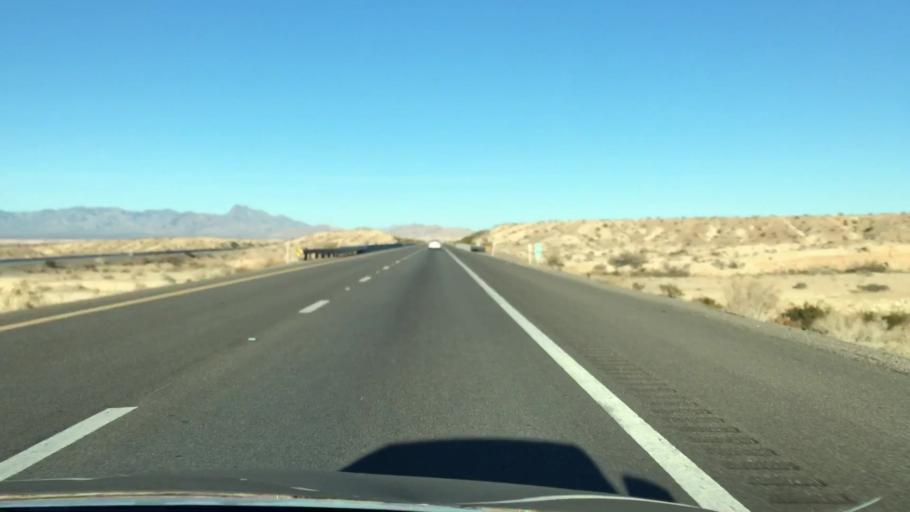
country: US
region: Nevada
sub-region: Clark County
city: Moapa Town
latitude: 36.6071
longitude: -114.6318
